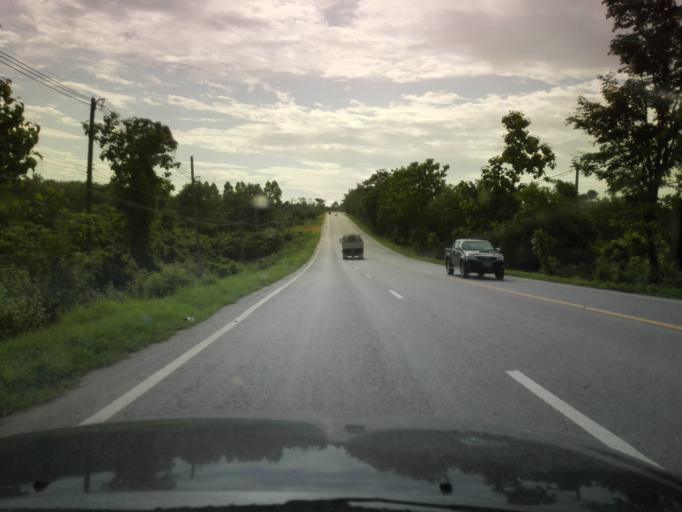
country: TH
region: Tak
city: Mae Ramat
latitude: 16.9718
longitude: 98.5358
